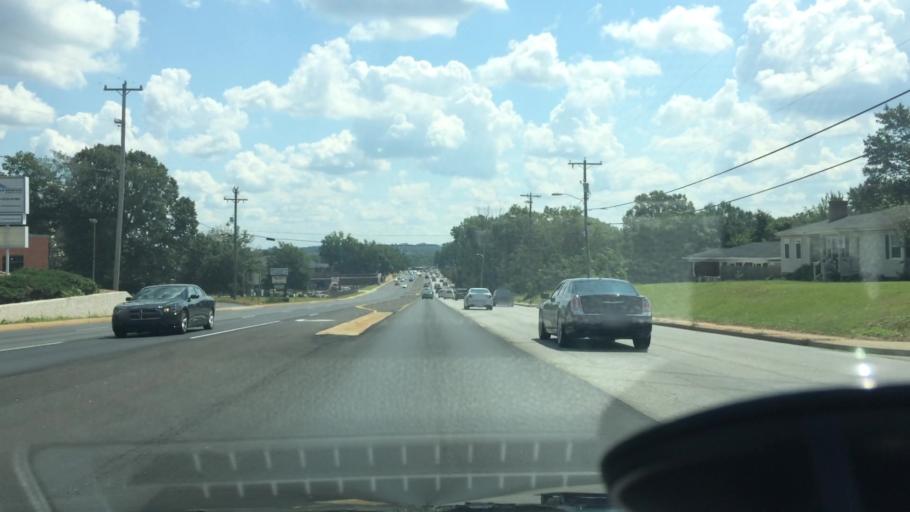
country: US
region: South Carolina
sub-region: Greenville County
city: Wade Hampton
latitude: 34.8837
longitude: -82.3677
